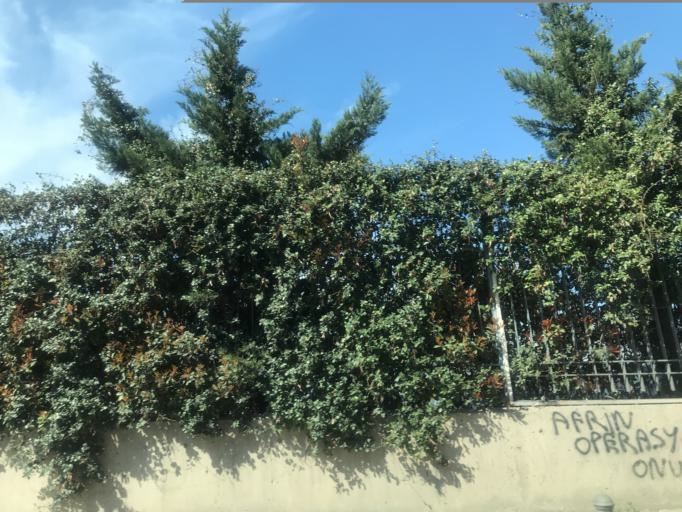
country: TR
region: Istanbul
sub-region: Atasehir
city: Atasehir
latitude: 40.9698
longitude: 29.1072
